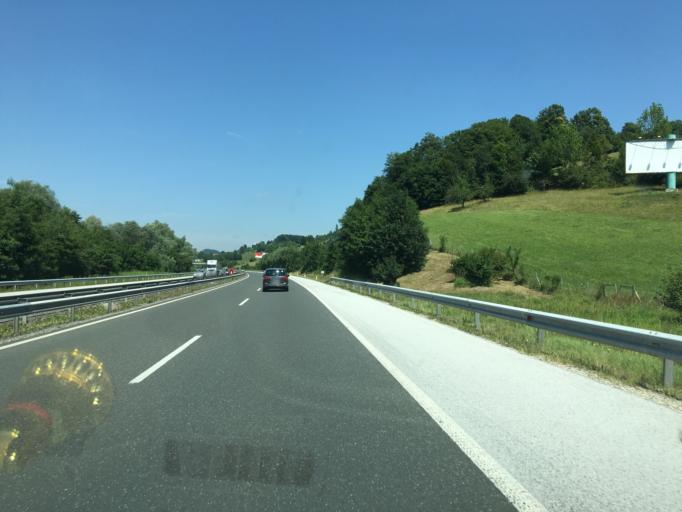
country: SI
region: Pesnica
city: Pesnica pri Mariboru
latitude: 46.6317
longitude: 15.6578
